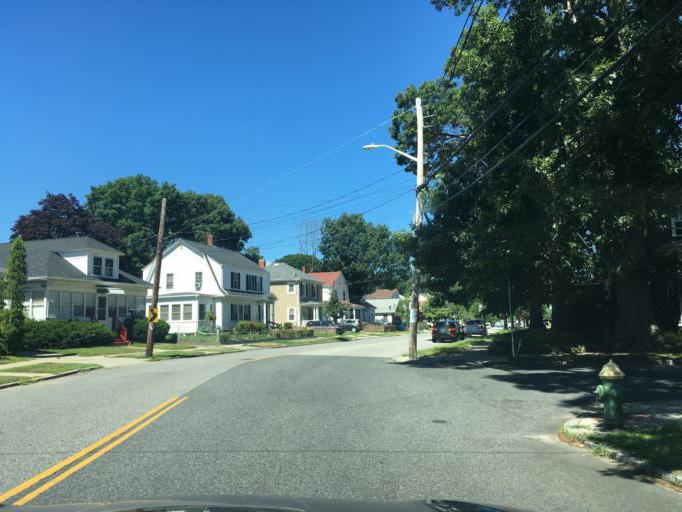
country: US
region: Rhode Island
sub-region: Providence County
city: Cranston
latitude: 41.7886
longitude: -71.4270
